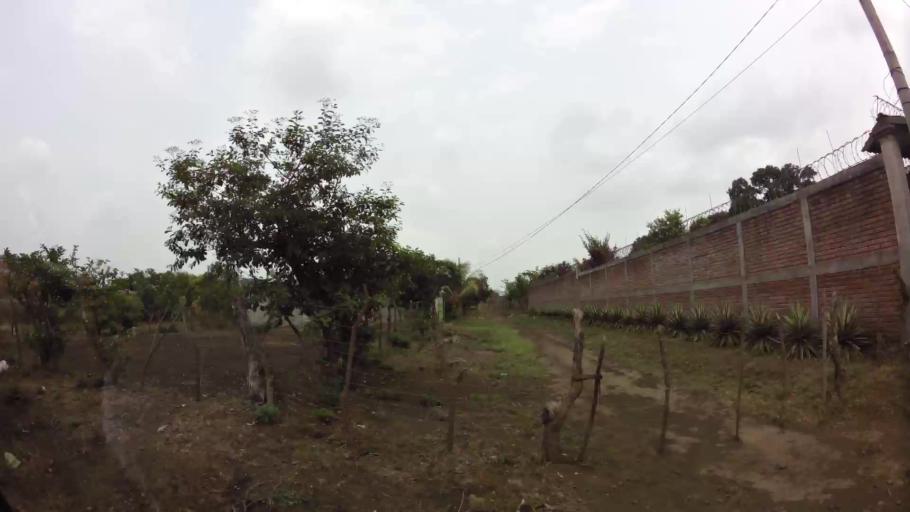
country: NI
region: Chinandega
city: Chinandega
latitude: 12.6245
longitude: -87.1112
